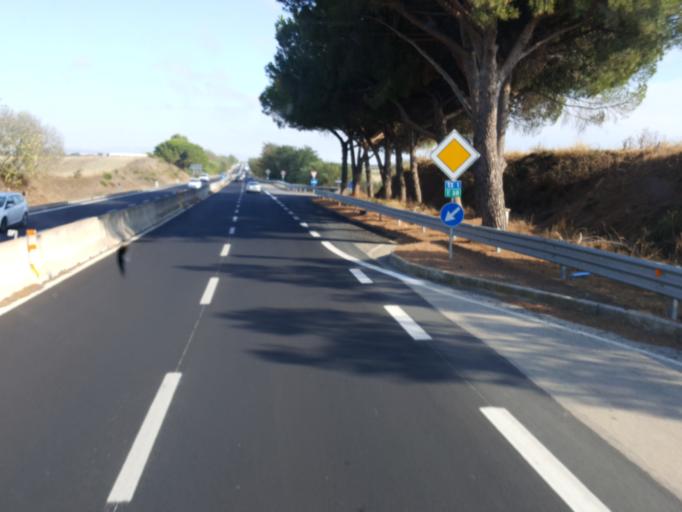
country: IT
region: Latium
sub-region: Provincia di Viterbo
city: Montalto di Castro
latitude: 42.3385
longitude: 11.6196
